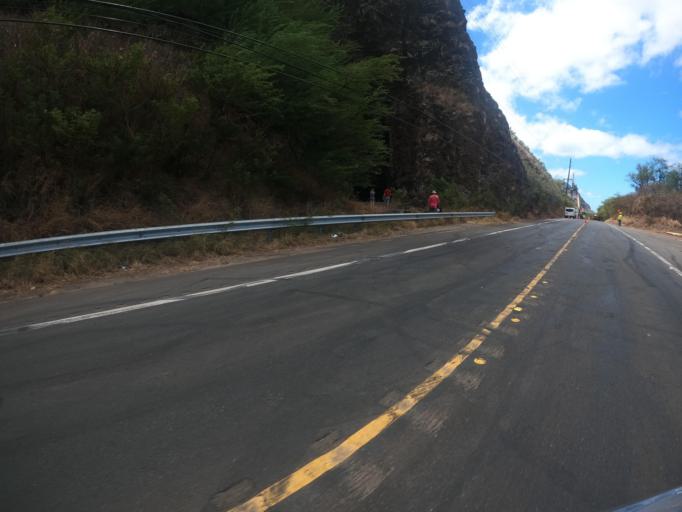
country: US
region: Hawaii
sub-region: Honolulu County
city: Makaha Valley
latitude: 21.5199
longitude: -158.2277
